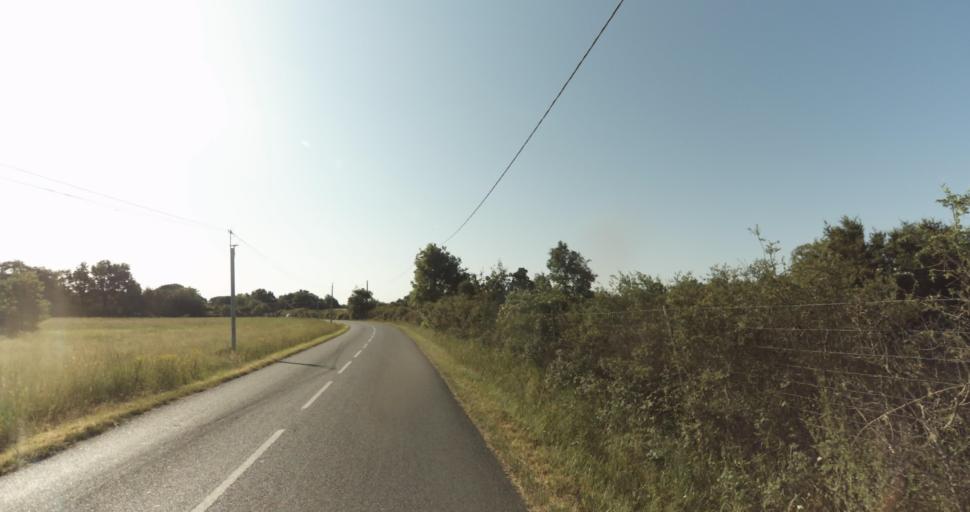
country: FR
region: Midi-Pyrenees
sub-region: Departement de la Haute-Garonne
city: Leguevin
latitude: 43.5761
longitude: 1.2299
